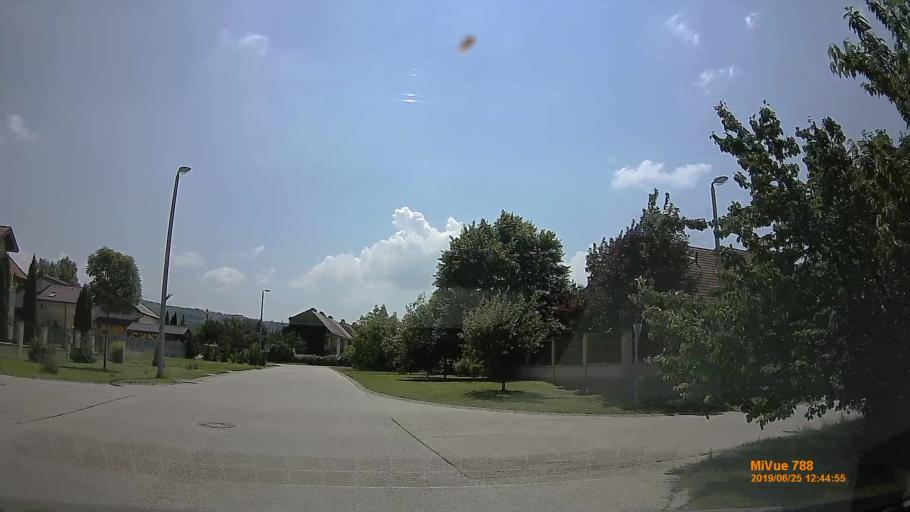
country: HU
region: Komarom-Esztergom
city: Esztergom
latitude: 47.8090
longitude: 18.7461
